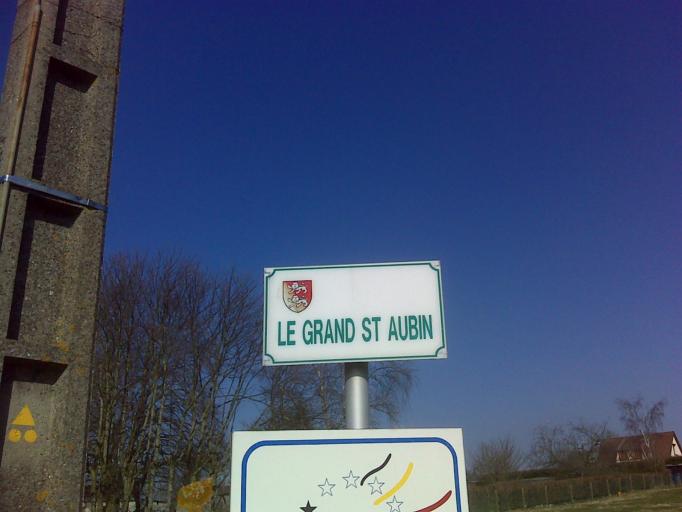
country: FR
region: Haute-Normandie
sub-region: Departement de l'Eure
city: Quillebeuf-sur-Seine
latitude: 49.4493
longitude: 0.5376
